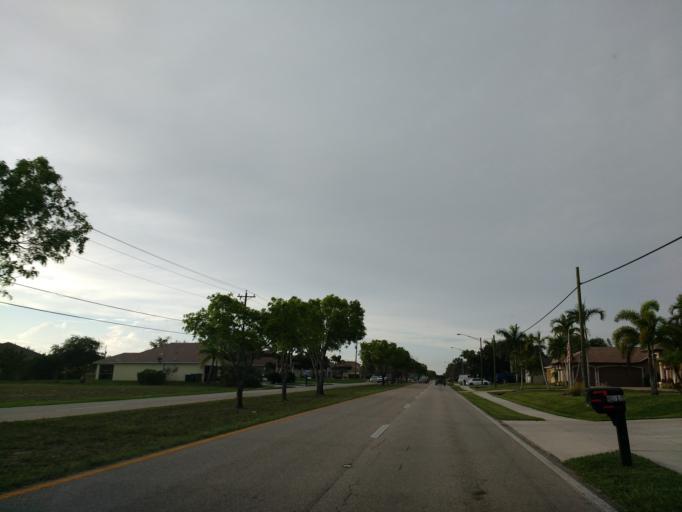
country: US
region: Florida
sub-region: Lee County
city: Cape Coral
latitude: 26.5750
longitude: -82.0068
